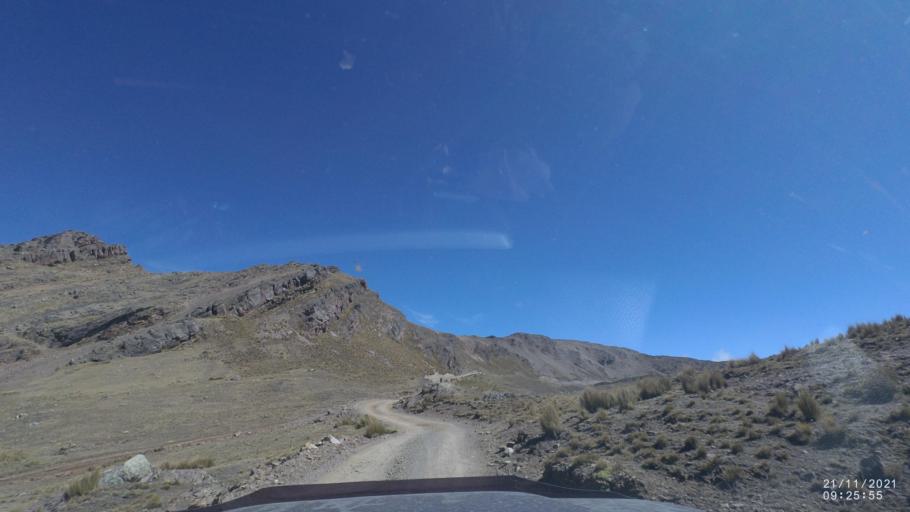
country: BO
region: Cochabamba
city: Cochabamba
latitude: -17.0897
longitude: -66.2544
